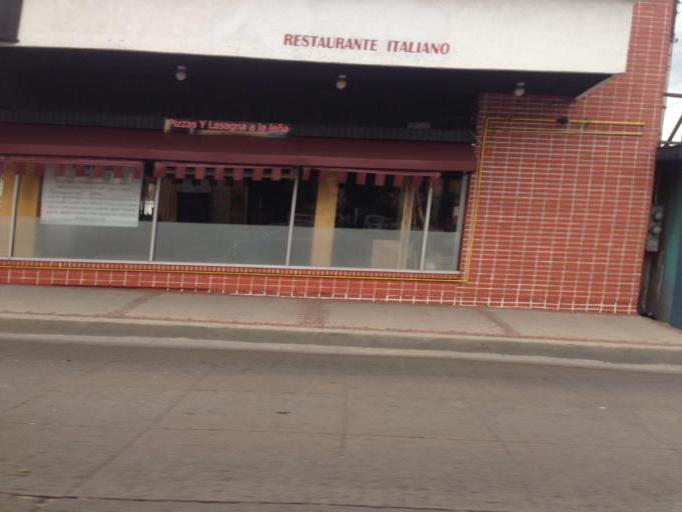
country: MX
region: Baja California
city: Tijuana
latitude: 32.5231
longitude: -117.0314
